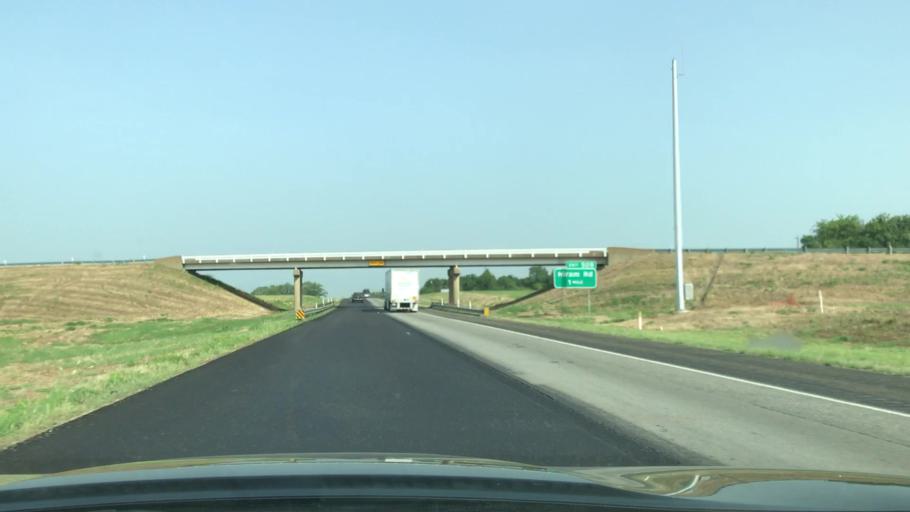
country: US
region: Texas
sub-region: Van Zandt County
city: Wills Point
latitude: 32.6641
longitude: -96.1253
